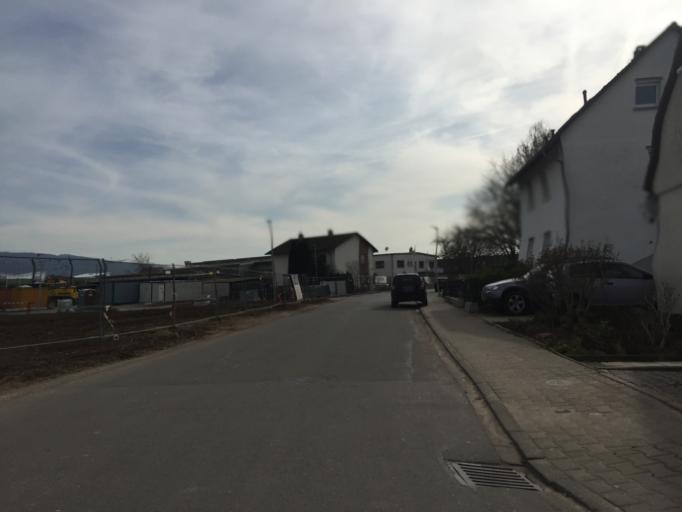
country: DE
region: Baden-Wuerttemberg
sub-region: Karlsruhe Region
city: Weinheim
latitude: 49.5298
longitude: 8.6499
